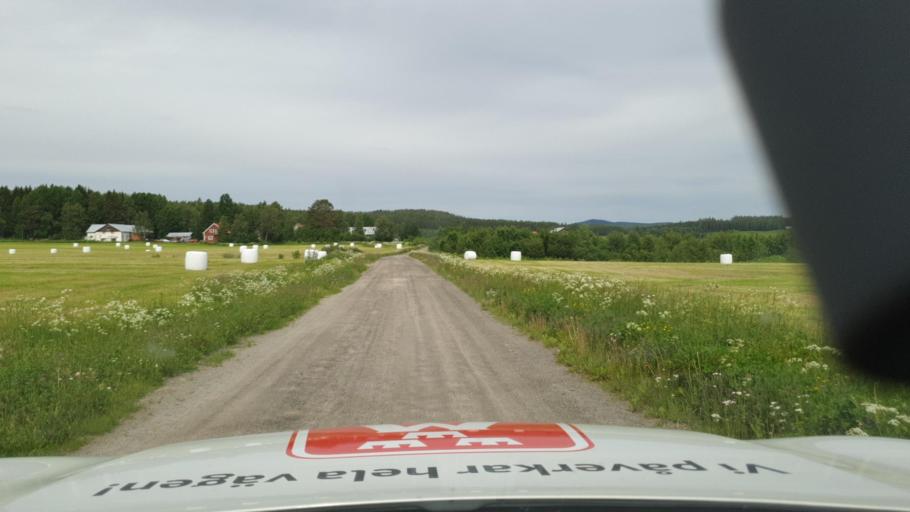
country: SE
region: Vaesterbotten
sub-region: Robertsfors Kommun
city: Robertsfors
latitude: 64.2668
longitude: 20.6152
